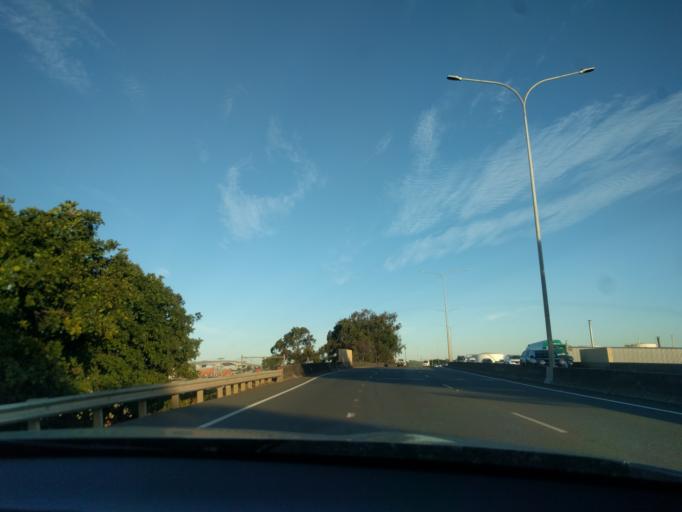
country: AU
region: Queensland
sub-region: Brisbane
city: Ascot
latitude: -27.4303
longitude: 153.0815
